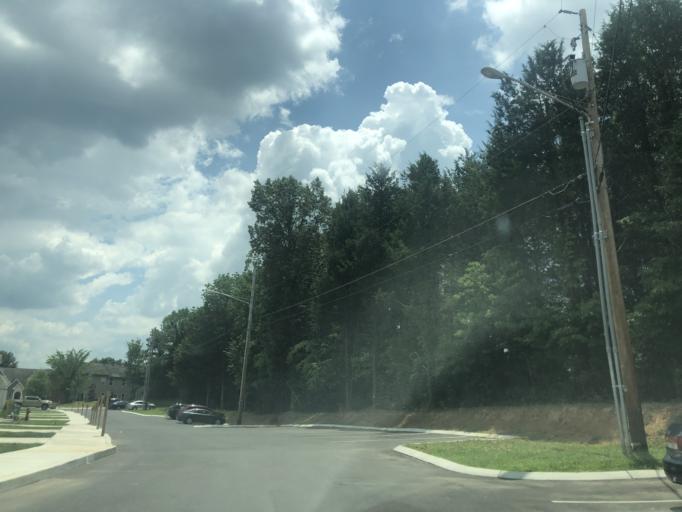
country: US
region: Tennessee
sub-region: Rutherford County
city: La Vergne
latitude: 36.0609
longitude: -86.6528
